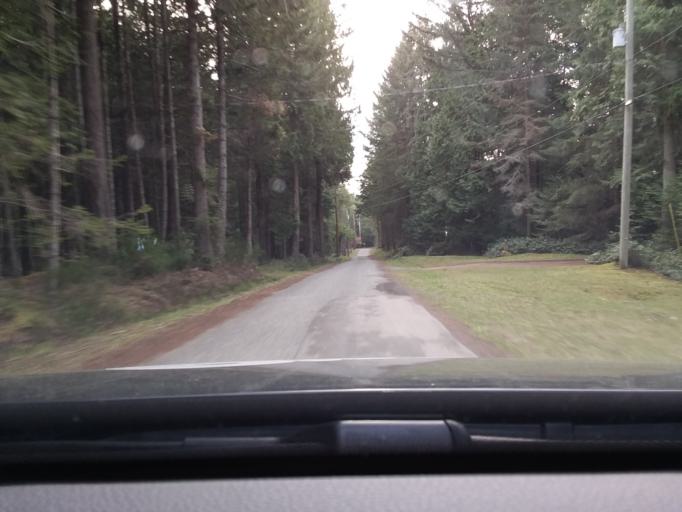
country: CA
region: British Columbia
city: North Saanich
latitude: 48.8742
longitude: -123.3298
